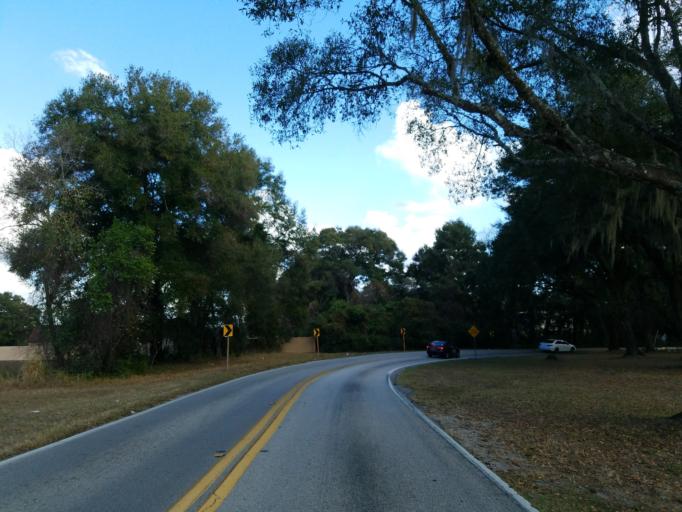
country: US
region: Florida
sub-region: Hillsborough County
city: Brandon
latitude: 27.9524
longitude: -82.3049
